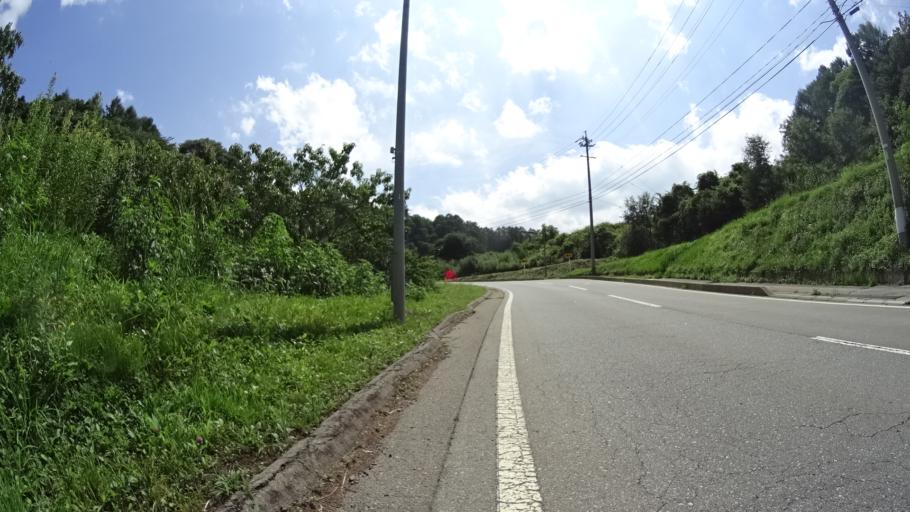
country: JP
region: Nagano
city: Saku
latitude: 36.0555
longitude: 138.4636
